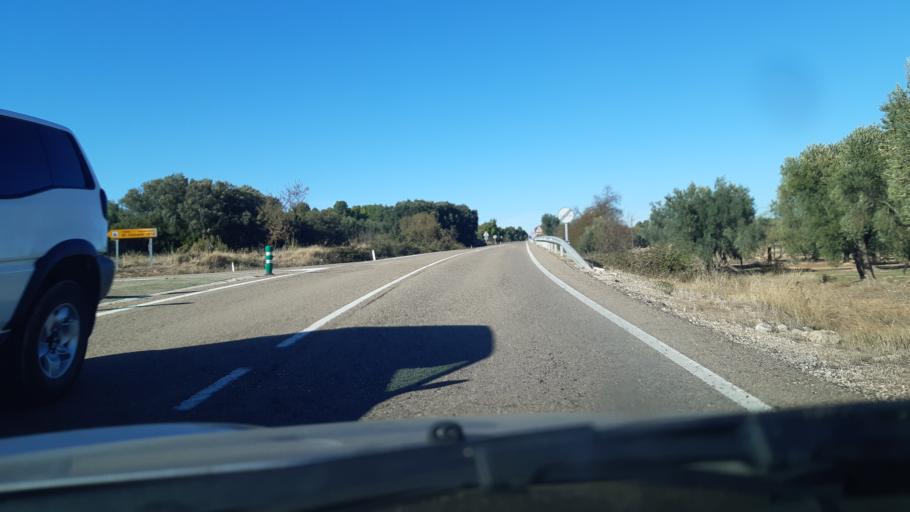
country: ES
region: Aragon
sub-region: Provincia de Teruel
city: Torre del Compte
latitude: 40.9108
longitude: 0.0833
